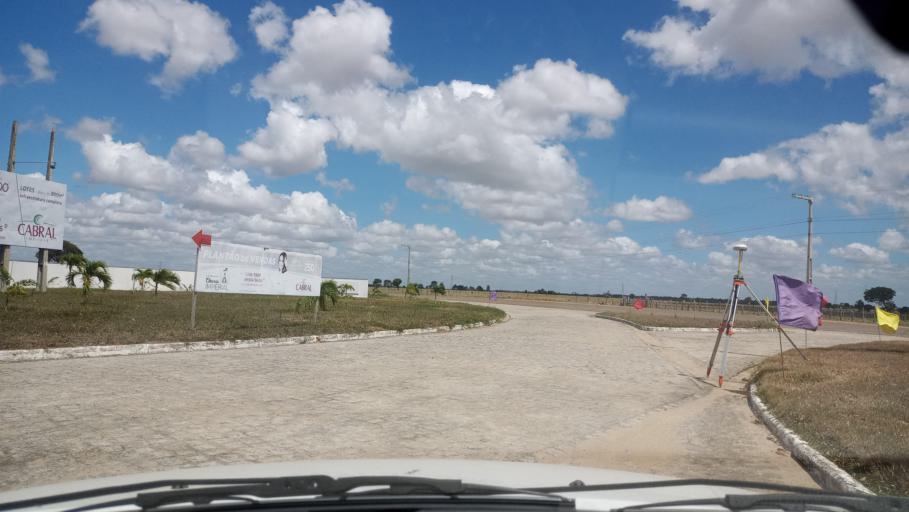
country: BR
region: Rio Grande do Norte
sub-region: Brejinho
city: Brejinho
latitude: -6.0383
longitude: -35.3910
